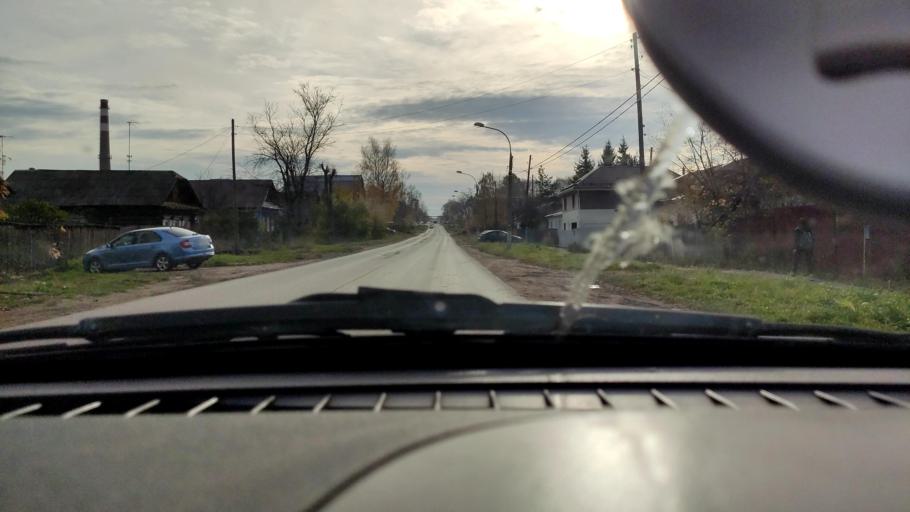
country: RU
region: Perm
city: Perm
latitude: 58.0914
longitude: 56.3861
